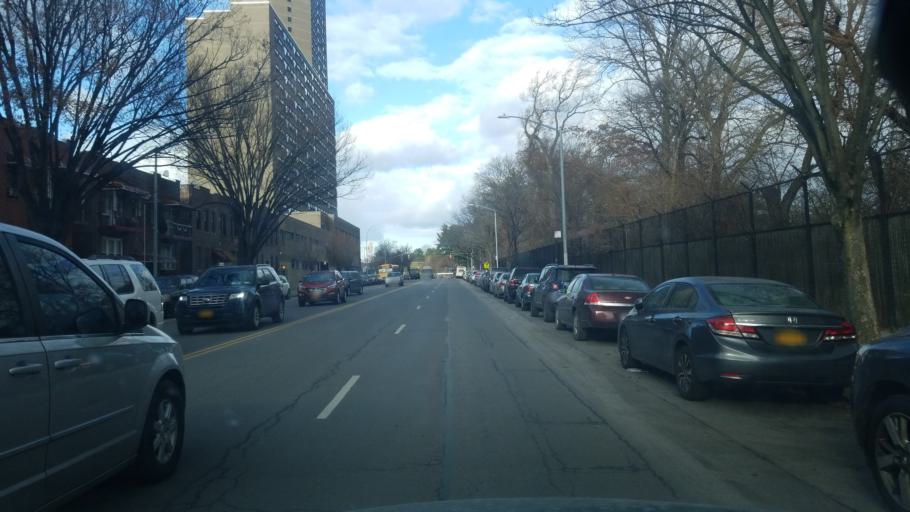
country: US
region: New York
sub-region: Bronx
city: The Bronx
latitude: 40.8542
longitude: -73.8814
